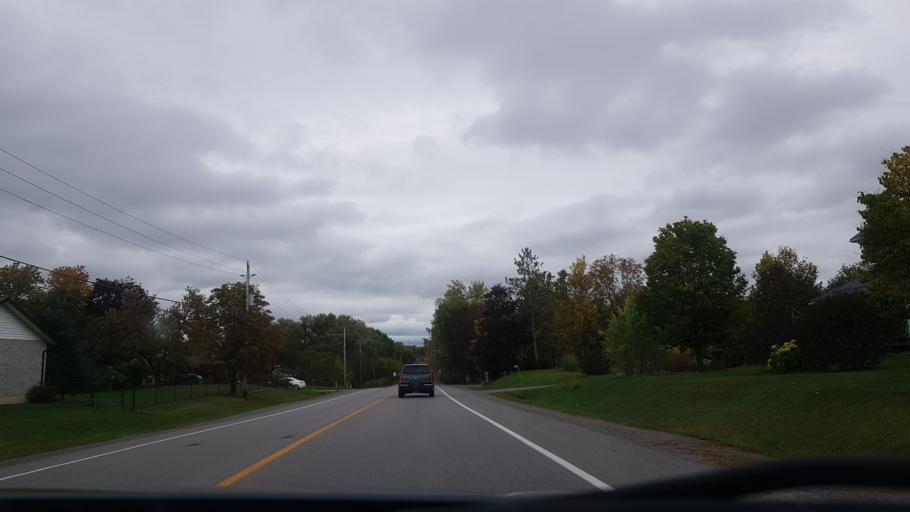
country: CA
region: Ontario
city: Omemee
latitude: 44.2042
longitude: -78.4706
